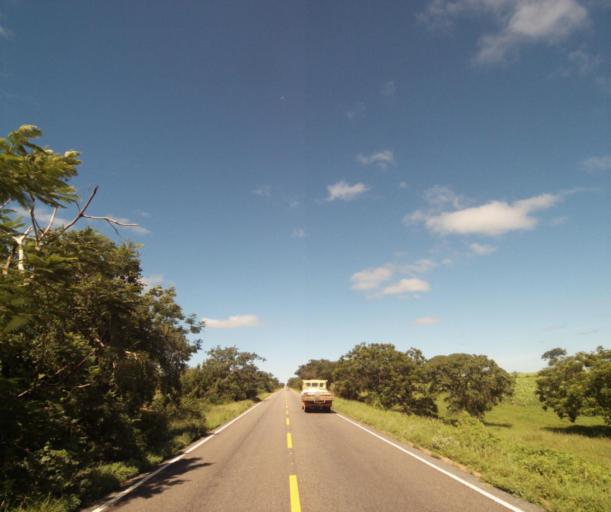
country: BR
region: Bahia
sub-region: Palmas De Monte Alto
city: Palmas de Monte Alto
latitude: -14.2420
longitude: -43.0692
